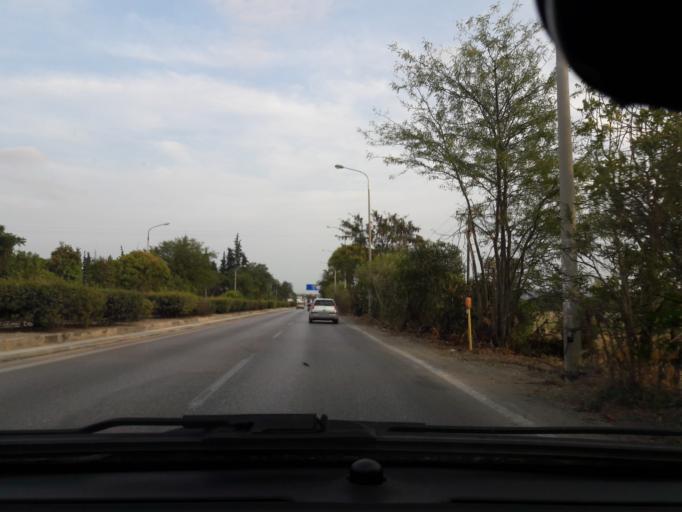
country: GR
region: Central Macedonia
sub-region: Nomos Thessalonikis
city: Thermi
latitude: 40.5362
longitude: 22.9922
